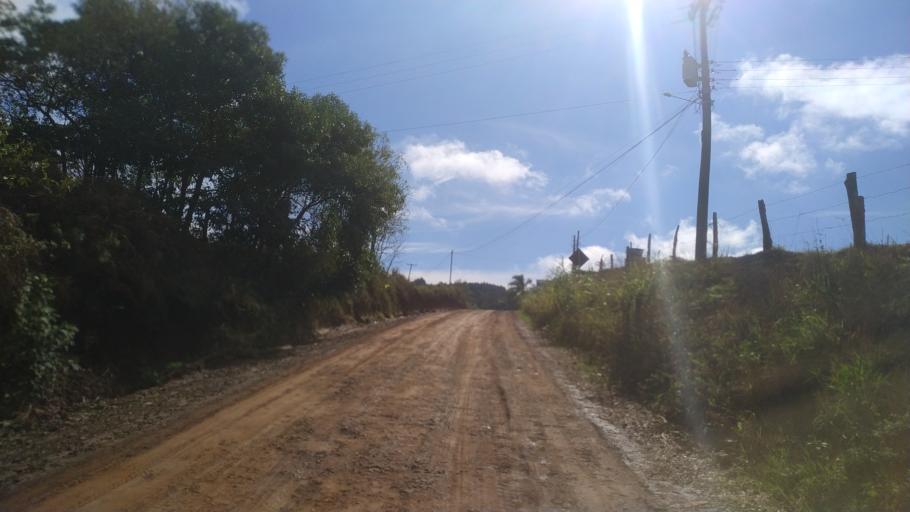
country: BR
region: Santa Catarina
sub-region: Chapeco
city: Chapeco
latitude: -27.1462
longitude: -52.5944
